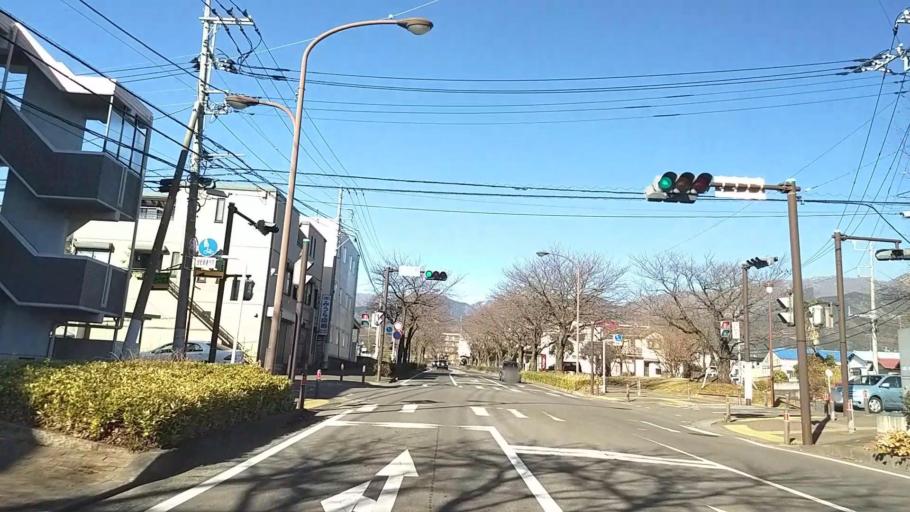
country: JP
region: Kanagawa
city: Hadano
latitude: 35.3846
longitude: 139.1843
